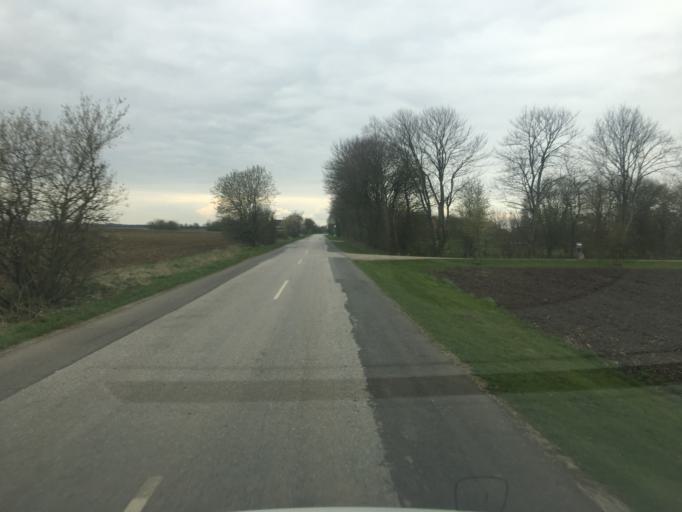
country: DK
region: South Denmark
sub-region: Aabenraa Kommune
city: Tinglev
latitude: 55.0277
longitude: 9.1686
